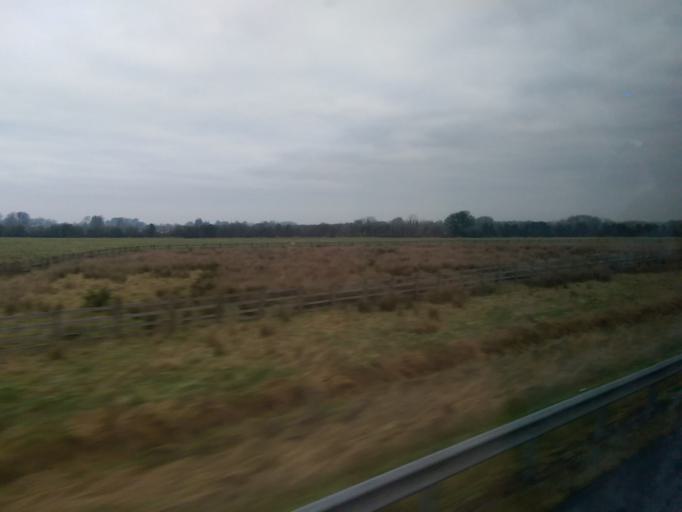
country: IE
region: Connaught
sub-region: County Galway
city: Ballinasloe
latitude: 53.2938
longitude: -8.3557
